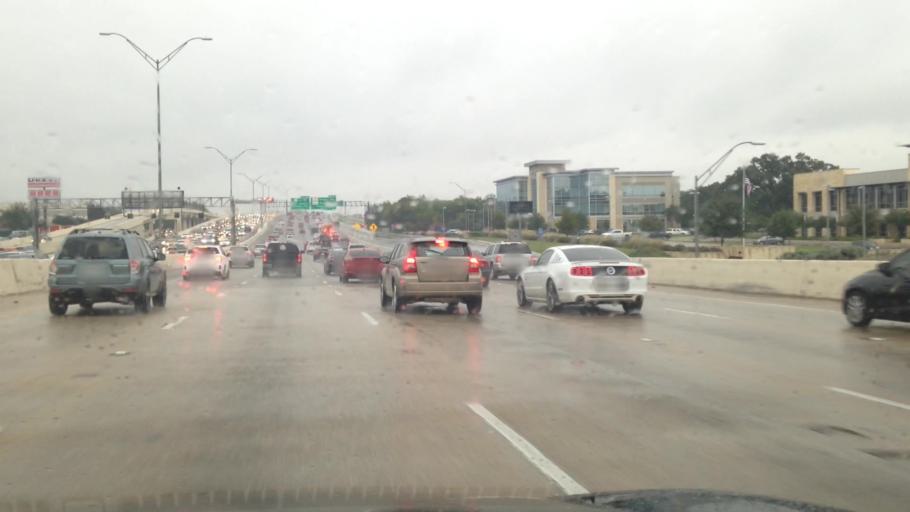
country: US
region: Texas
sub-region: Bexar County
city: Castle Hills
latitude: 29.5171
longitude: -98.5261
